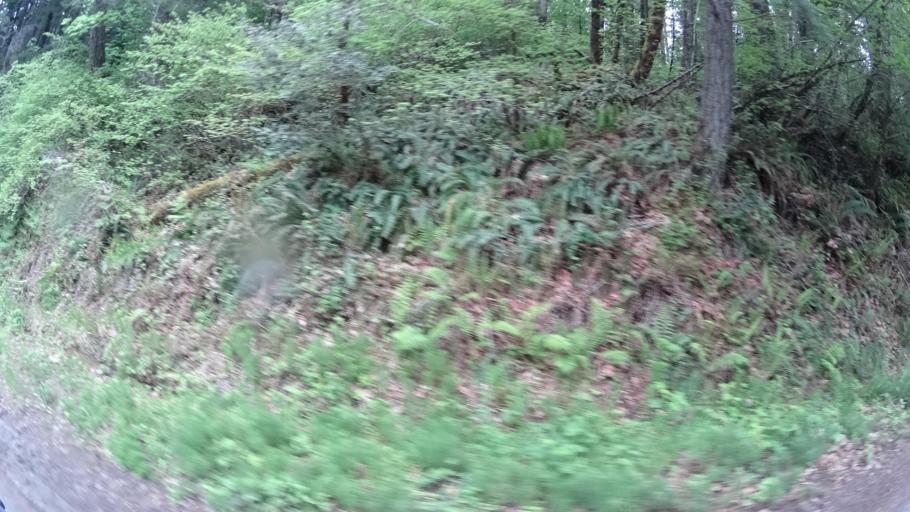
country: US
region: California
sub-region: Humboldt County
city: Willow Creek
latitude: 41.1246
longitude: -123.7480
